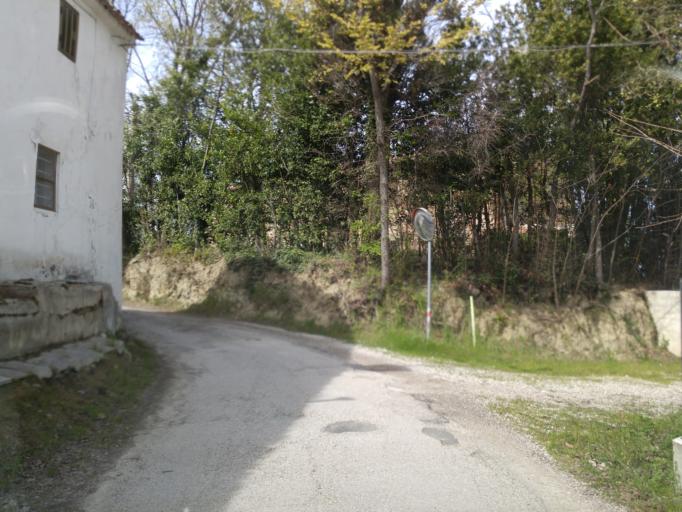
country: IT
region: The Marches
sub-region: Provincia di Pesaro e Urbino
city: Cartoceto
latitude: 43.7698
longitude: 12.8949
